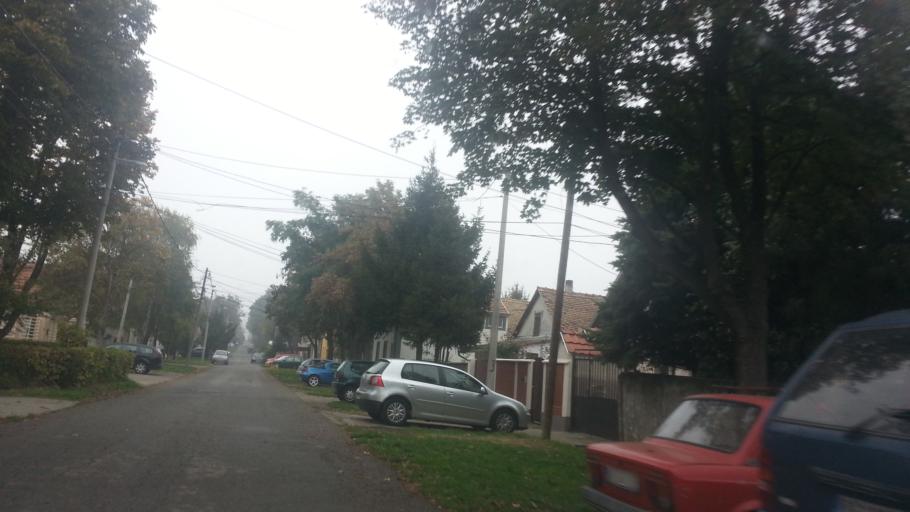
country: RS
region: Central Serbia
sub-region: Belgrade
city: Zemun
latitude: 44.8371
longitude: 20.3800
